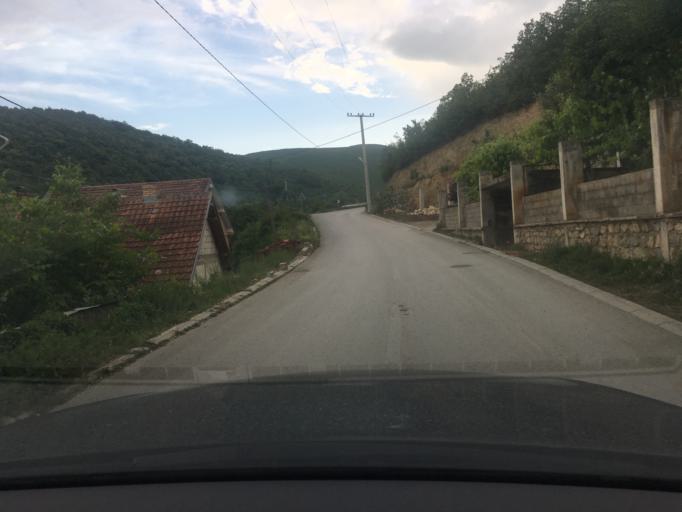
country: XK
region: Ferizaj
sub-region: Hani i Elezit
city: Hani i Elezit
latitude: 42.1451
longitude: 21.2894
